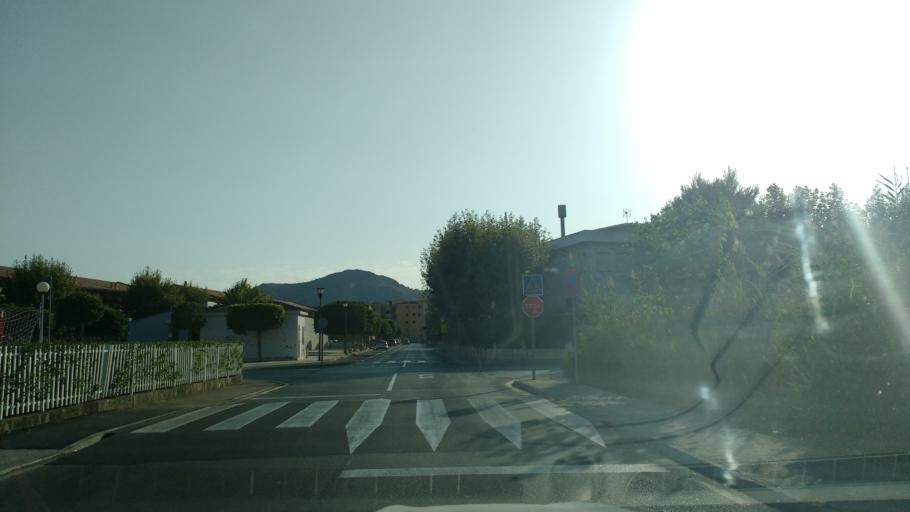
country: ES
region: Balearic Islands
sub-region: Illes Balears
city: Port d'Alcudia
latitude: 39.8417
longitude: 3.1255
